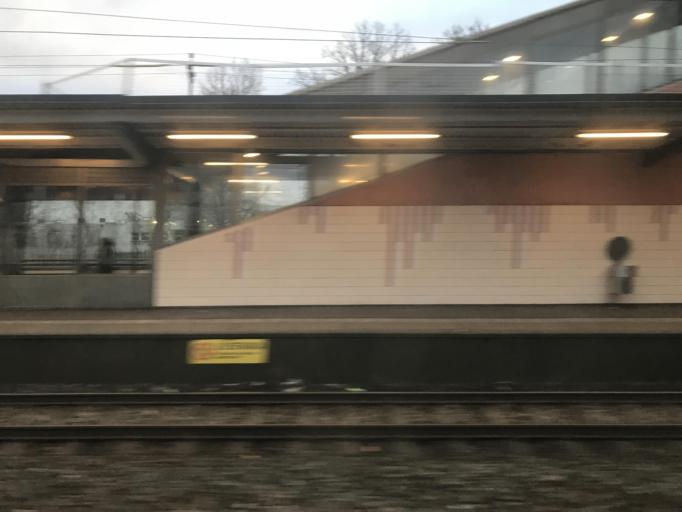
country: SE
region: Stockholm
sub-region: Stockholms Kommun
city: Arsta
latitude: 59.2787
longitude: 18.0118
